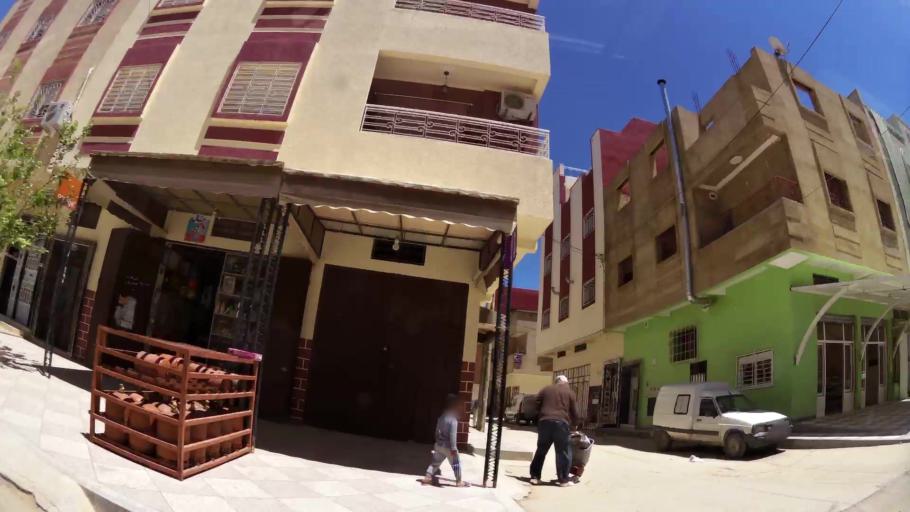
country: MA
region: Meknes-Tafilalet
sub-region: Meknes
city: Meknes
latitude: 33.8643
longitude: -5.5630
